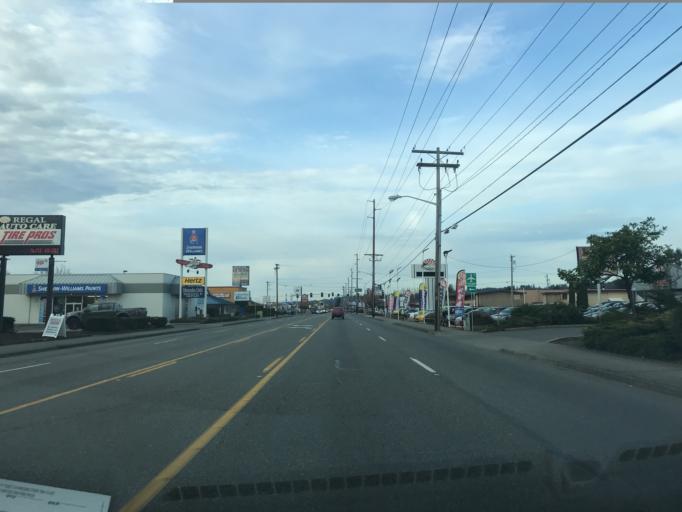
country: US
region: Washington
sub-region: King County
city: Auburn
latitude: 47.3247
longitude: -122.2215
